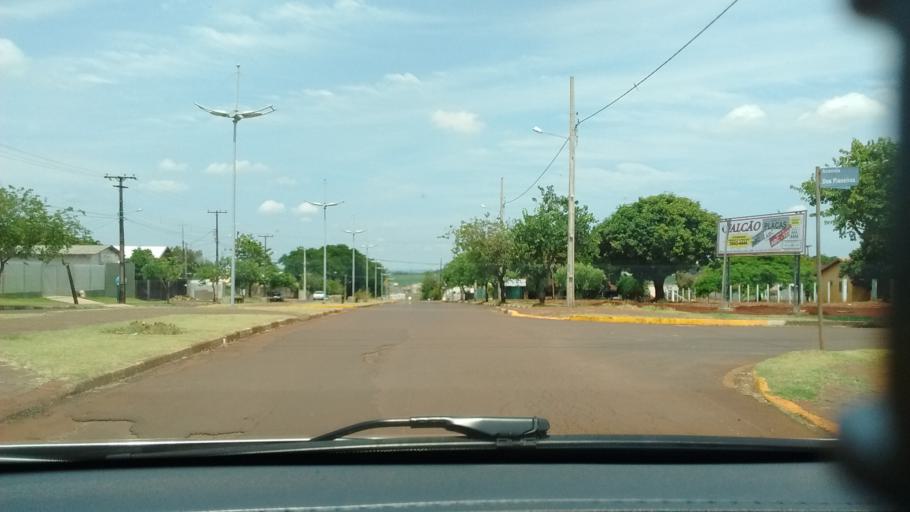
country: BR
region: Parana
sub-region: Corbelia
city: Corbelia
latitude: -24.5502
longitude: -52.9861
